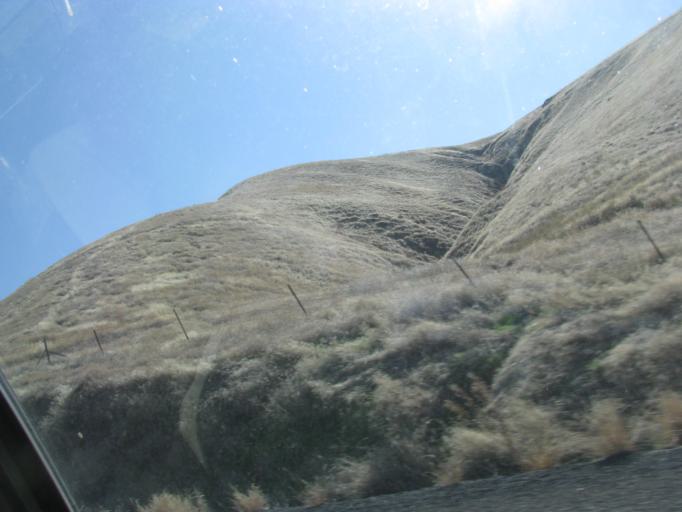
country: US
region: Washington
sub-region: Asotin County
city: Asotin
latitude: 46.3191
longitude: -117.0520
